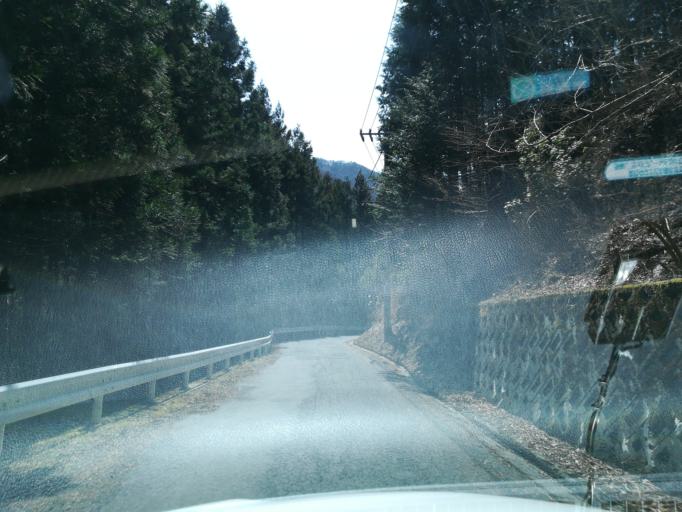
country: JP
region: Tokushima
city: Wakimachi
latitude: 33.8626
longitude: 134.0682
